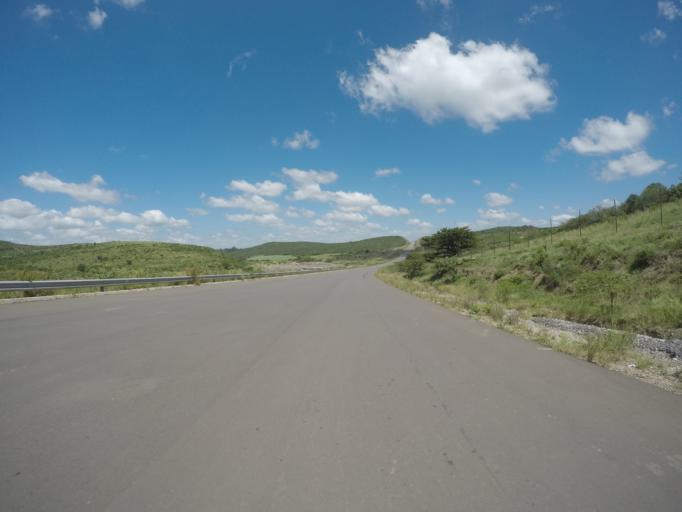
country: ZA
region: KwaZulu-Natal
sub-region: uThungulu District Municipality
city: Empangeni
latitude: -28.6157
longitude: 31.7546
